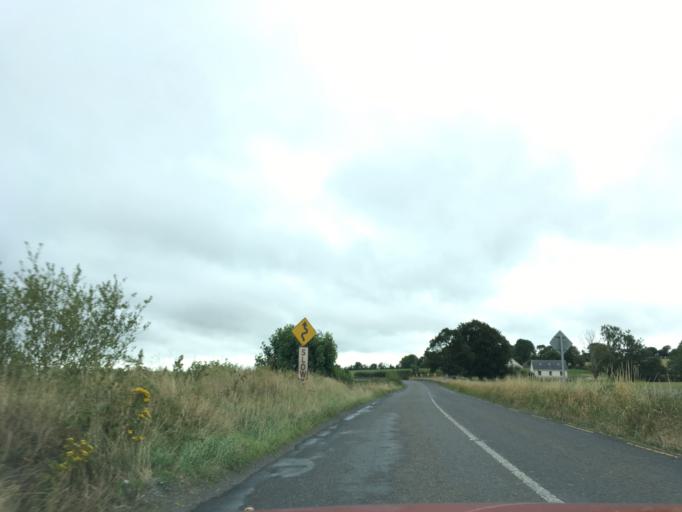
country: IE
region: Munster
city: Cashel
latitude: 52.4545
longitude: -7.8163
